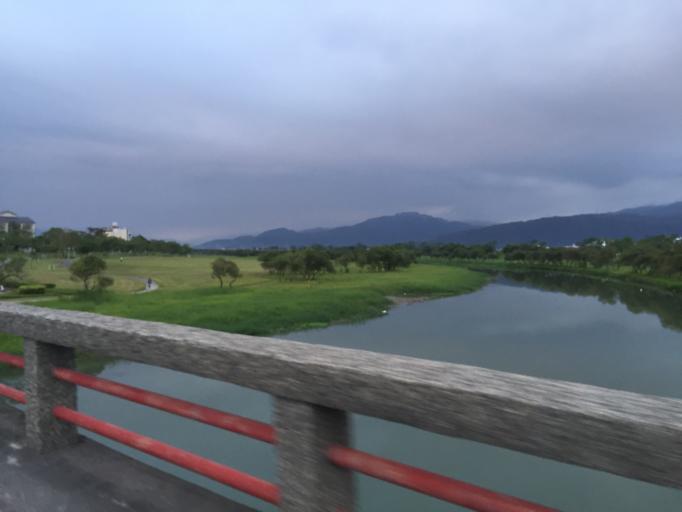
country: TW
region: Taiwan
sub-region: Yilan
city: Yilan
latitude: 24.7661
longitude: 121.7553
